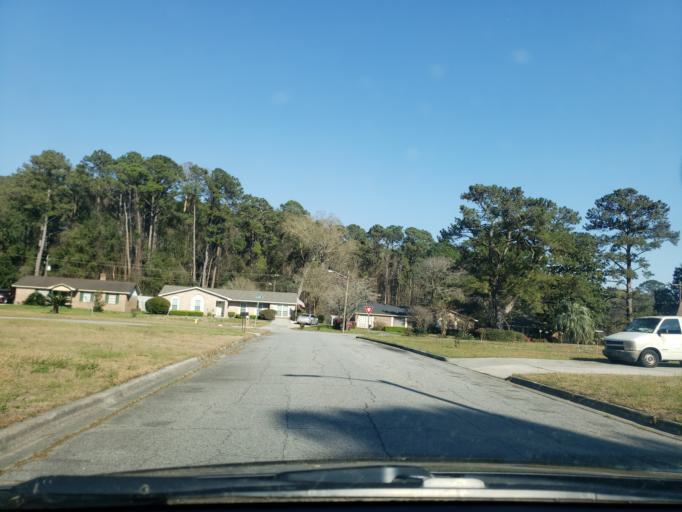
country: US
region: Georgia
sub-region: Chatham County
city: Montgomery
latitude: 31.9893
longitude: -81.1538
